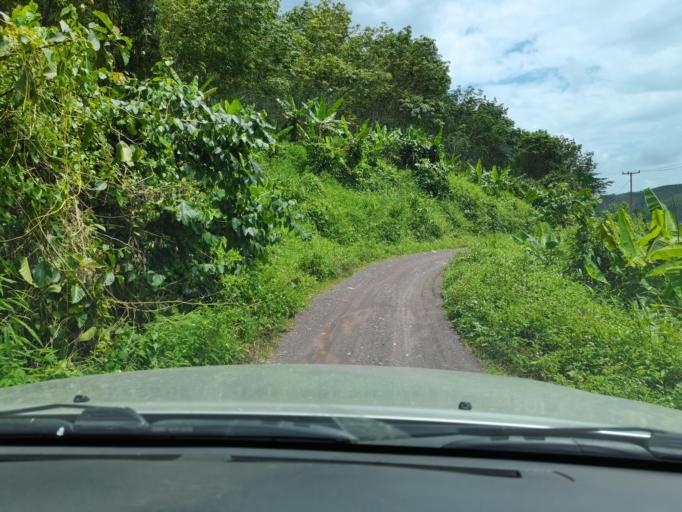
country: LA
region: Loungnamtha
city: Muang Long
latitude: 20.7136
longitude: 101.0136
